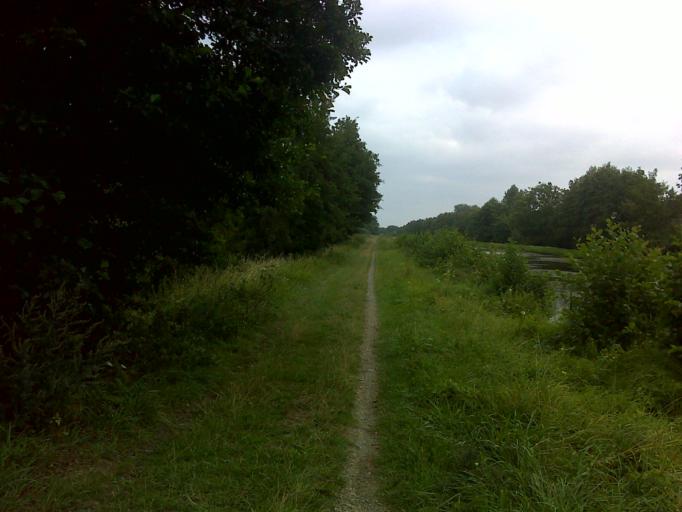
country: FR
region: Nord-Pas-de-Calais
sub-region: Departement du Nord
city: Bousies
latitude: 50.1000
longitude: 3.6360
